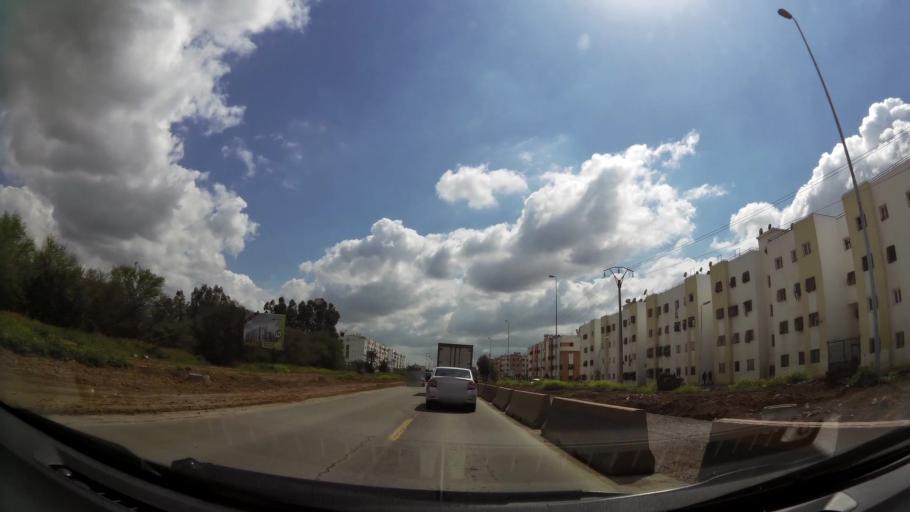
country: MA
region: Chaouia-Ouardigha
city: Nouaseur
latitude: 33.3659
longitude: -7.5443
